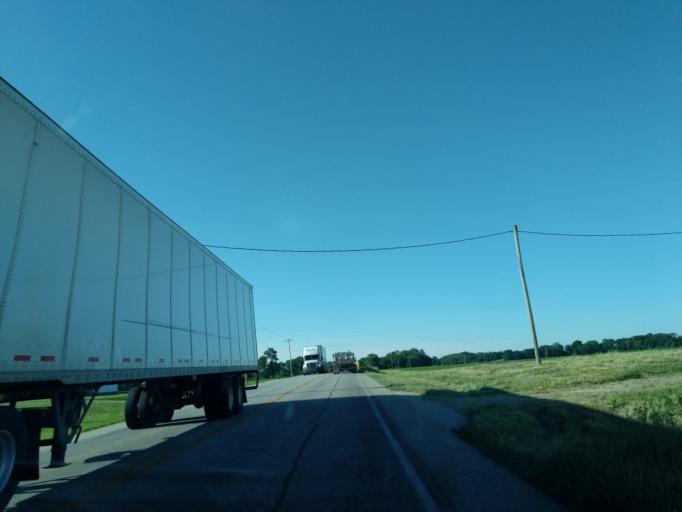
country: US
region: Indiana
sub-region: Shelby County
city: Morristown
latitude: 39.6160
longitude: -85.7671
